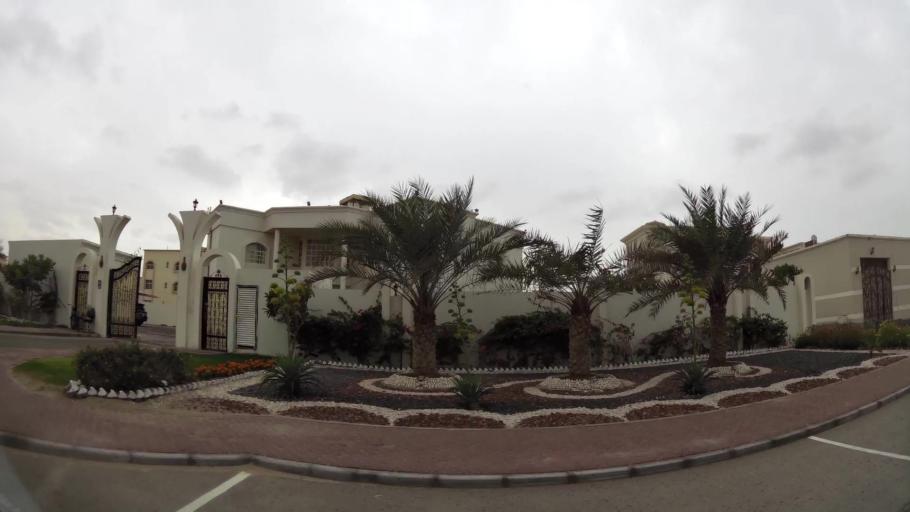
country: AE
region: Abu Dhabi
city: Abu Dhabi
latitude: 24.3743
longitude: 54.6465
